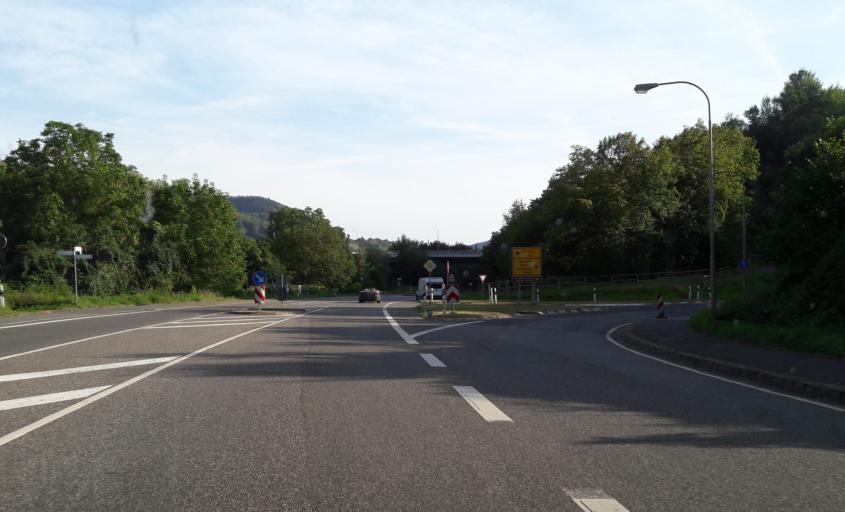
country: DE
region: Rheinland-Pfalz
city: Bruttig-Fankel
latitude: 50.1410
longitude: 7.2346
